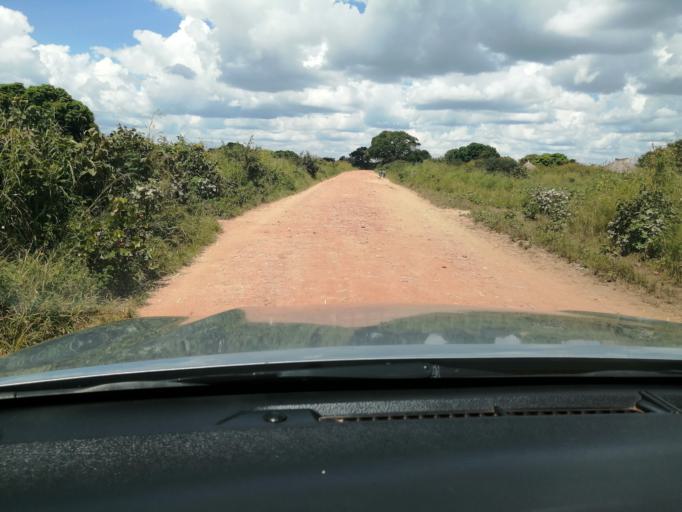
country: ZM
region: Lusaka
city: Lusaka
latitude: -15.1912
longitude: 27.9572
